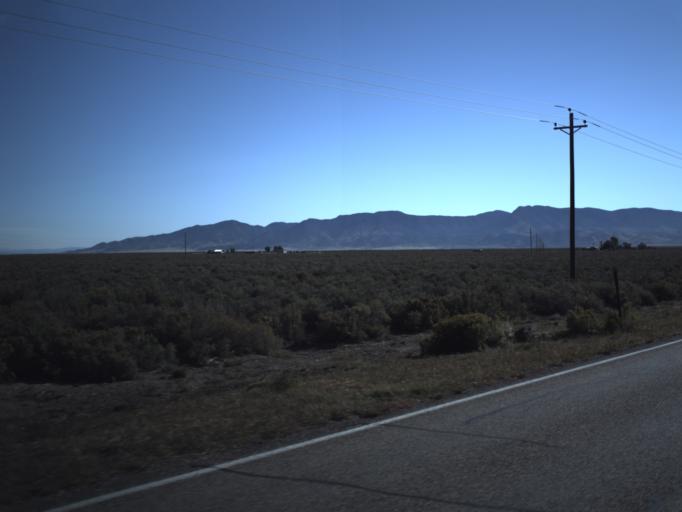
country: US
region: Utah
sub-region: Washington County
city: Enterprise
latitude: 37.7025
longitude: -113.6369
